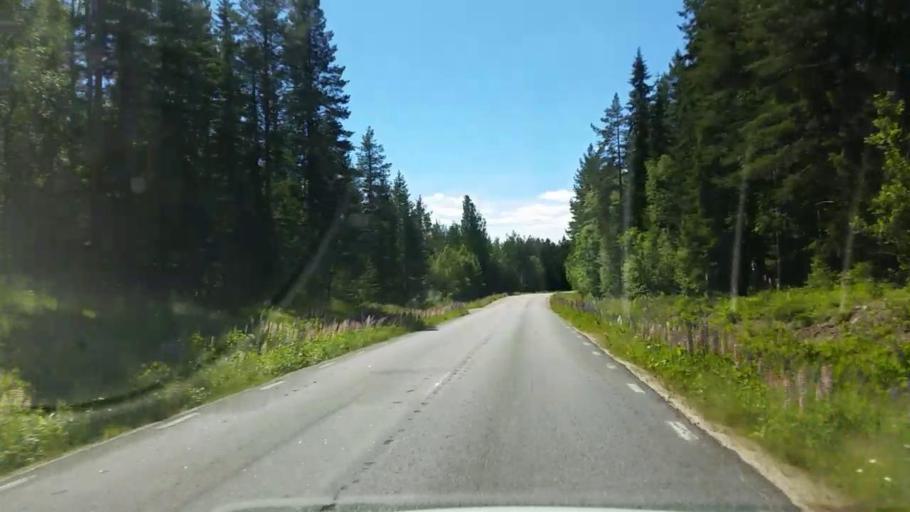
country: SE
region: Gaevleborg
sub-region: Ljusdals Kommun
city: Farila
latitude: 61.6806
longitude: 15.6421
